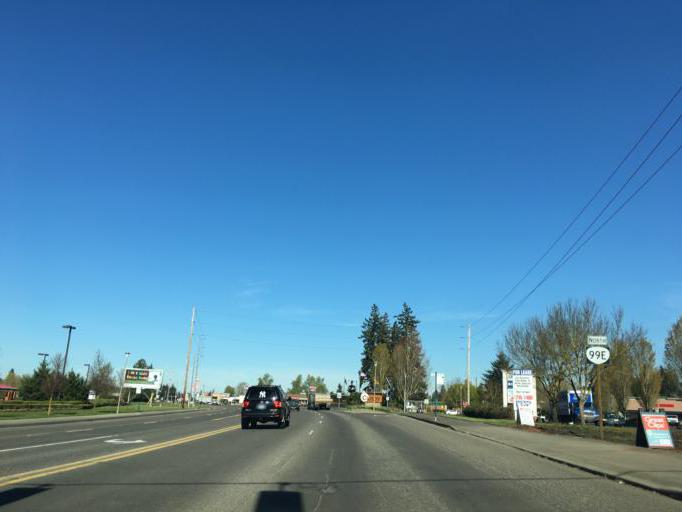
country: US
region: Oregon
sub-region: Clackamas County
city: Canby
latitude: 45.2564
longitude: -122.7040
